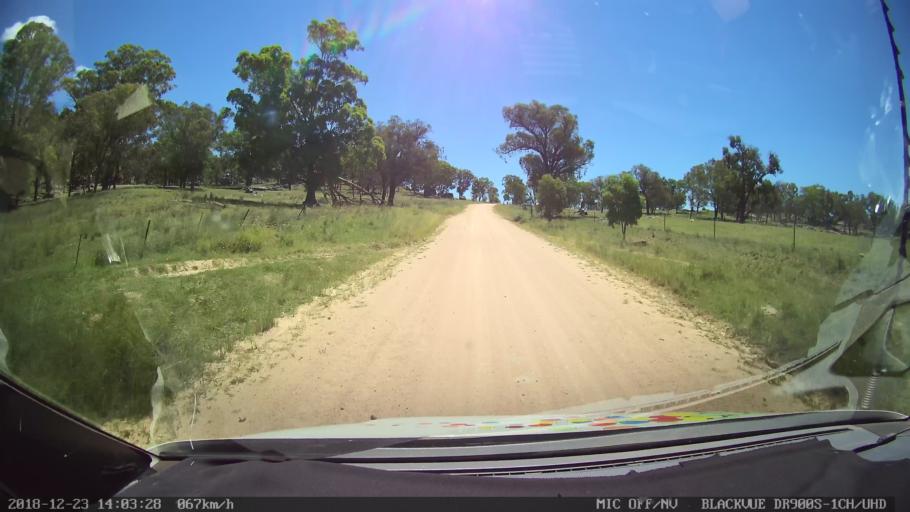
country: AU
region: New South Wales
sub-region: Tamworth Municipality
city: Manilla
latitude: -30.6234
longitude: 151.1001
